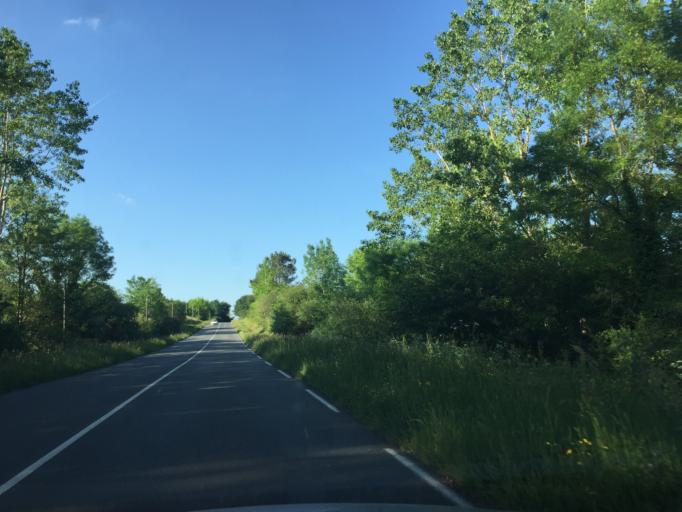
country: FR
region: Aquitaine
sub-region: Departement de la Dordogne
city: La Roche-Chalais
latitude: 45.1975
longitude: 0.0335
